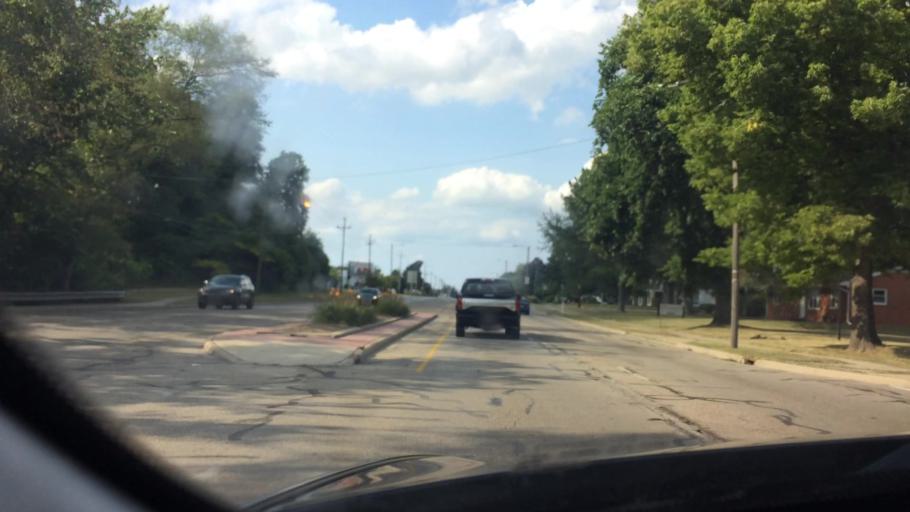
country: US
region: Ohio
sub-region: Lucas County
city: Holland
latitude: 41.6117
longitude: -83.6646
